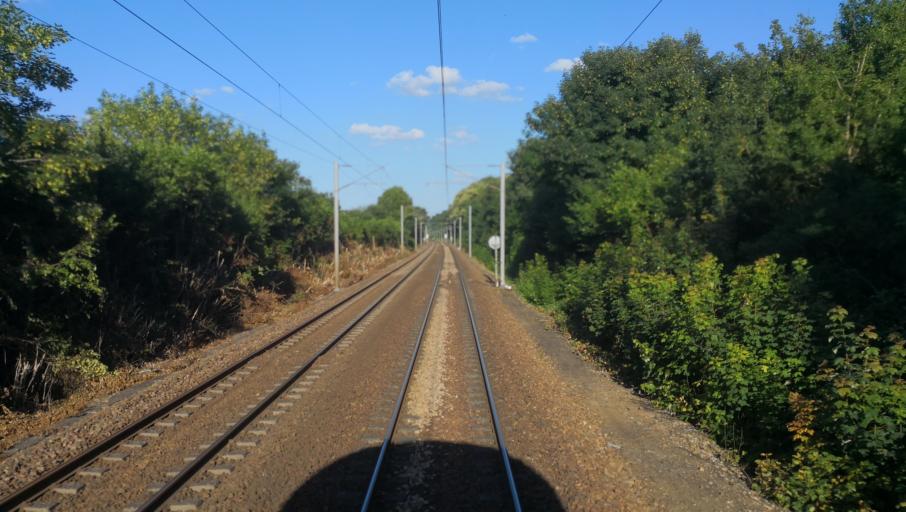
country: FR
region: Ile-de-France
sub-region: Departement des Yvelines
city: Rosny-sur-Seine
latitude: 48.9835
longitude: 1.6375
